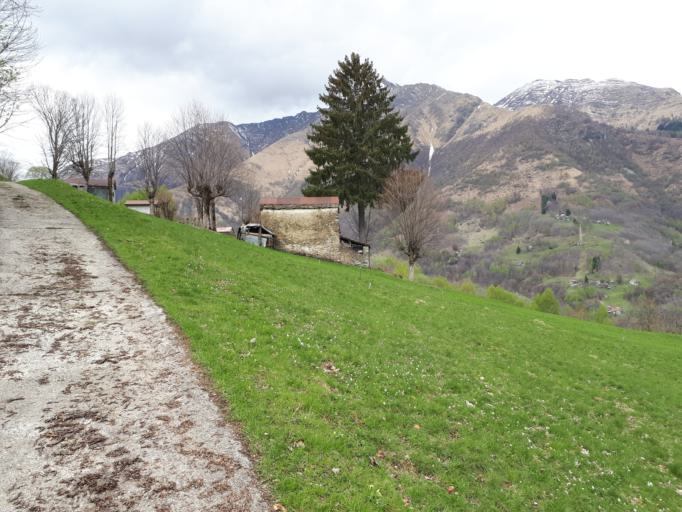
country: IT
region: Lombardy
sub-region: Provincia di Como
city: Garzeno
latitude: 46.1623
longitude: 9.2349
